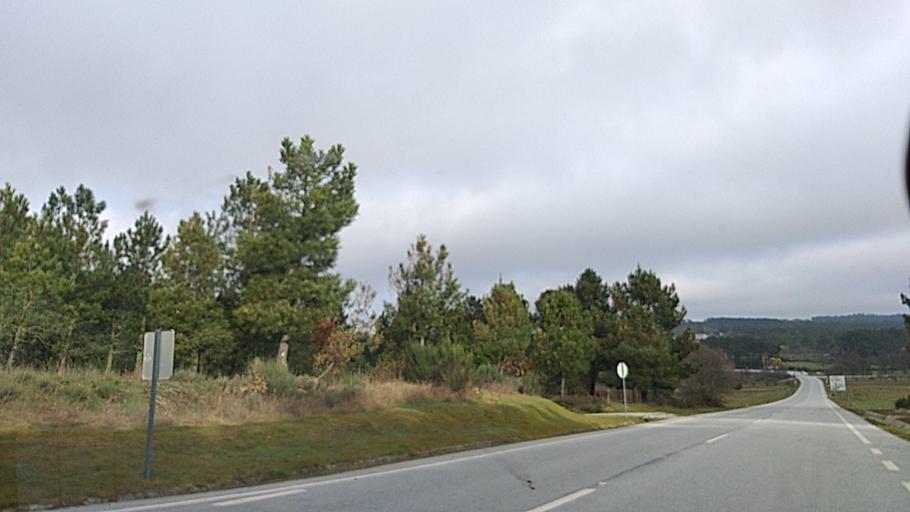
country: PT
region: Guarda
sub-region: Fornos de Algodres
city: Fornos de Algodres
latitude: 40.7143
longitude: -7.4868
